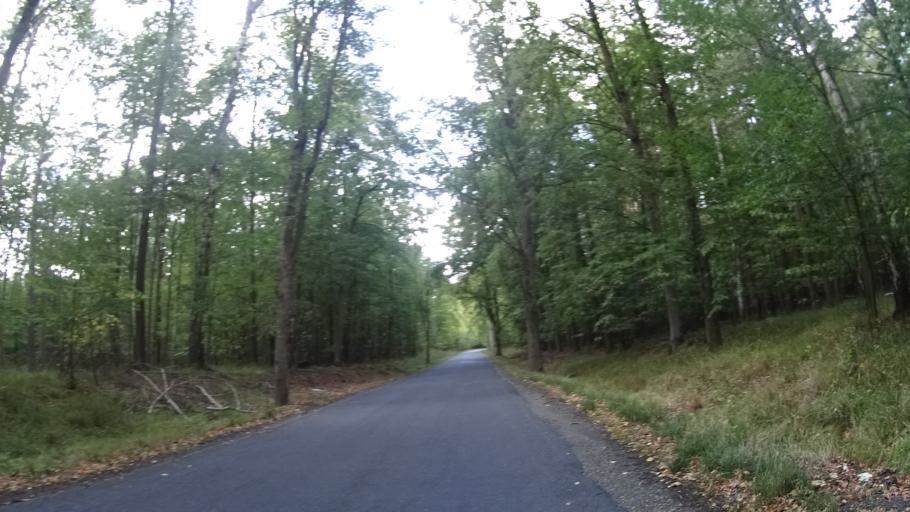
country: CZ
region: Olomoucky
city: Bila Lhota
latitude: 49.7289
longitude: 17.0118
